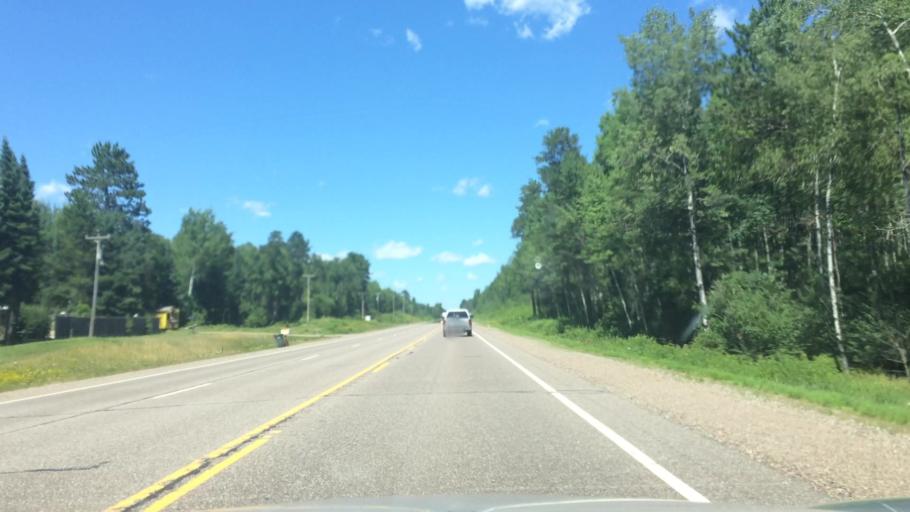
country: US
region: Wisconsin
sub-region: Lincoln County
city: Tomahawk
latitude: 45.6743
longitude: -89.7141
